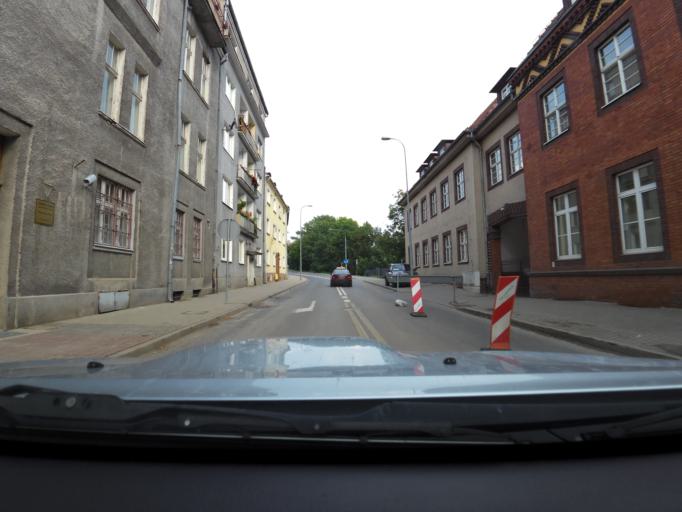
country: PL
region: Warmian-Masurian Voivodeship
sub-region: Powiat olsztynski
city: Olsztyn
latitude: 53.7768
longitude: 20.4798
